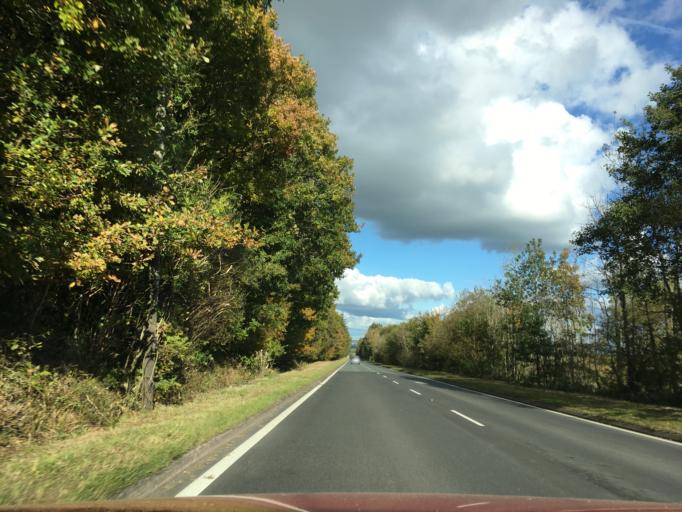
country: GB
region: Wales
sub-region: Sir Powys
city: Brecon
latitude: 51.9057
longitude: -3.4846
